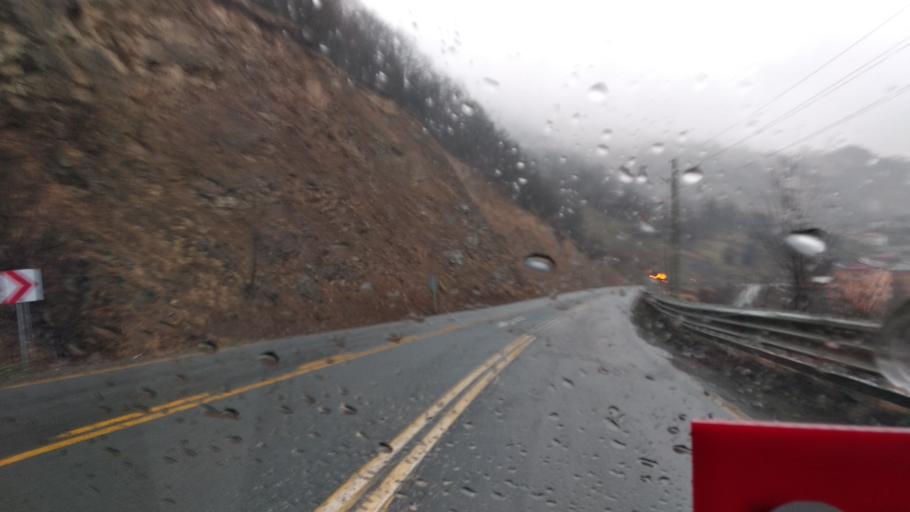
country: TR
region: Trabzon
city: Macka
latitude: 40.7068
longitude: 39.4930
